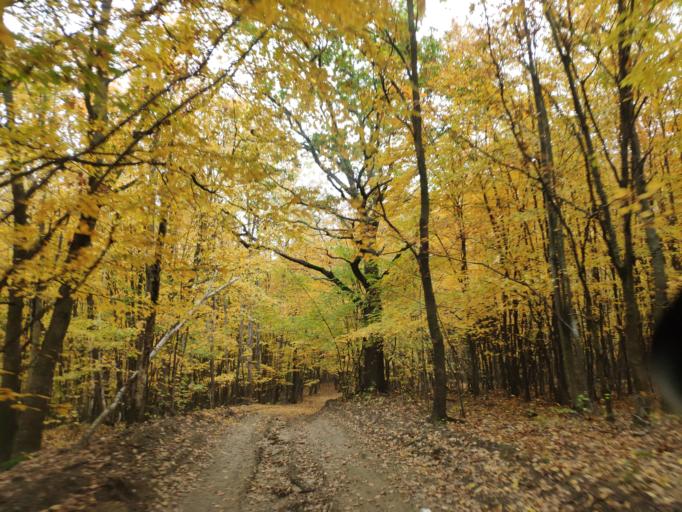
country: SK
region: Kosicky
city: Moldava nad Bodvou
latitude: 48.7154
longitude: 21.0121
